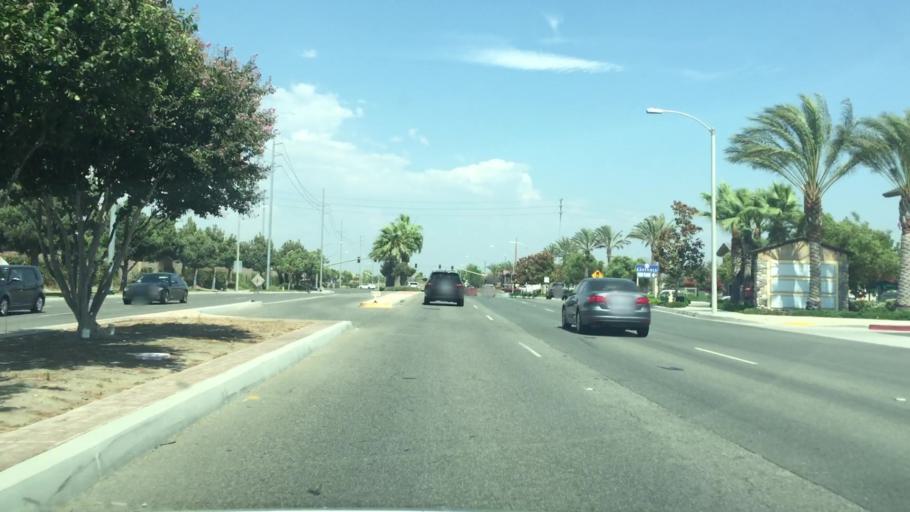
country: US
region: California
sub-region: Riverside County
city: Norco
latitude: 33.9608
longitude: -117.5956
